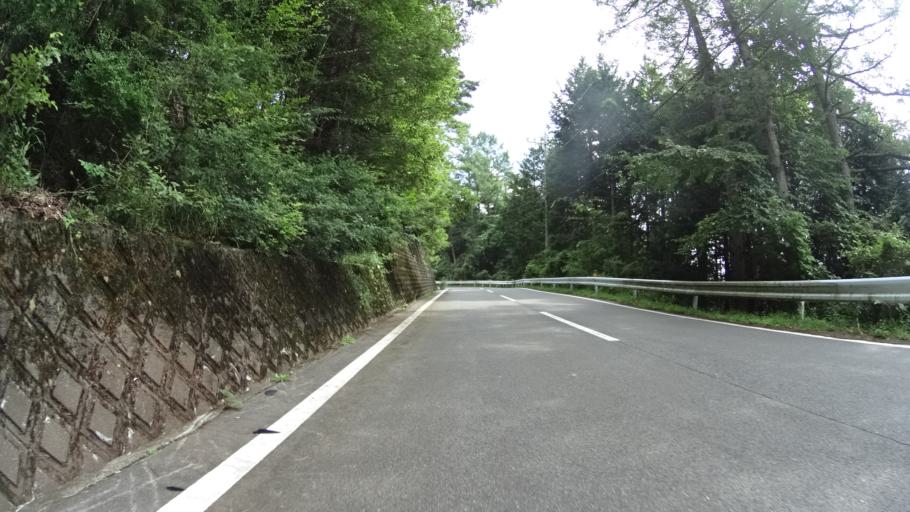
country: JP
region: Yamanashi
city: Kofu-shi
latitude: 35.7679
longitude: 138.5507
